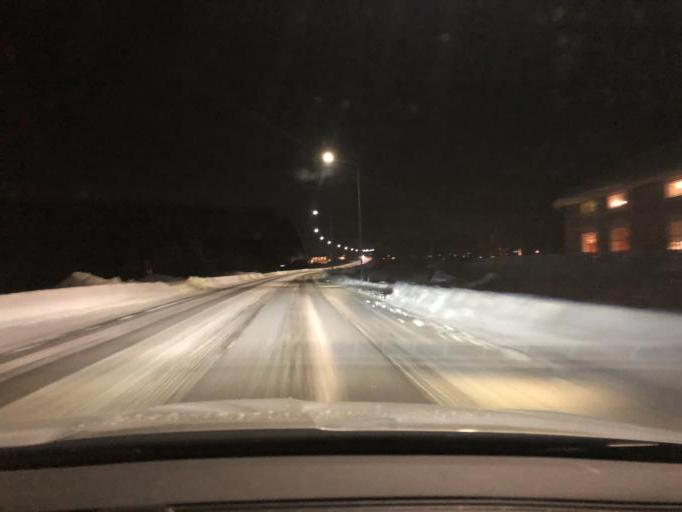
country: SE
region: Norrbotten
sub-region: Lulea Kommun
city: Bergnaset
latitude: 65.5816
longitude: 22.0510
